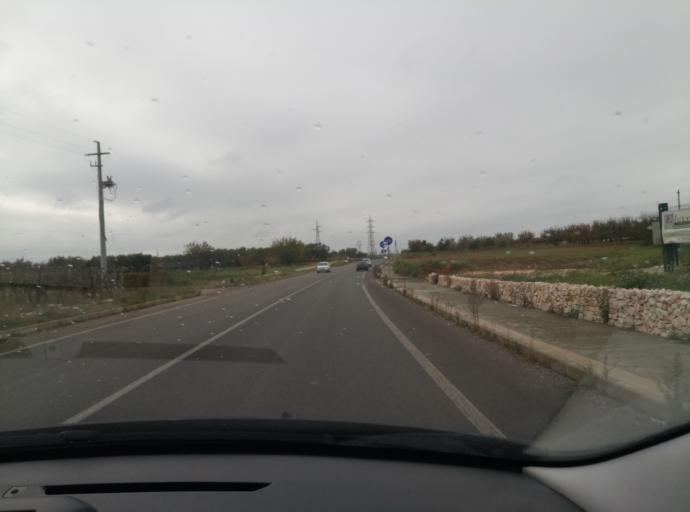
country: IT
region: Apulia
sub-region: Provincia di Bari
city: Acquaviva delle Fonti
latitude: 40.8904
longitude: 16.8291
